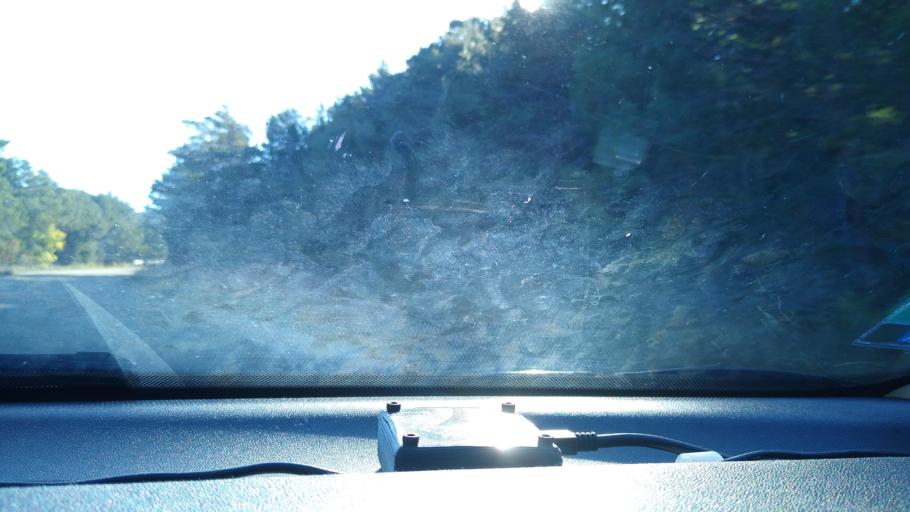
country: ES
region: Catalonia
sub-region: Provincia de Barcelona
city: Saldes
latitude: 42.2132
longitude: 1.7181
